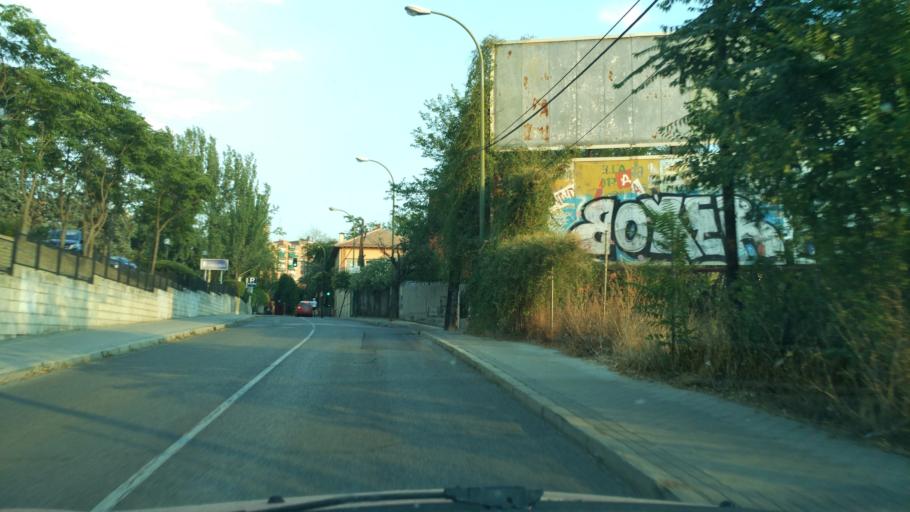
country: ES
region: Madrid
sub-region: Provincia de Madrid
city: Tetuan de las Victorias
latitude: 40.4687
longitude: -3.7253
